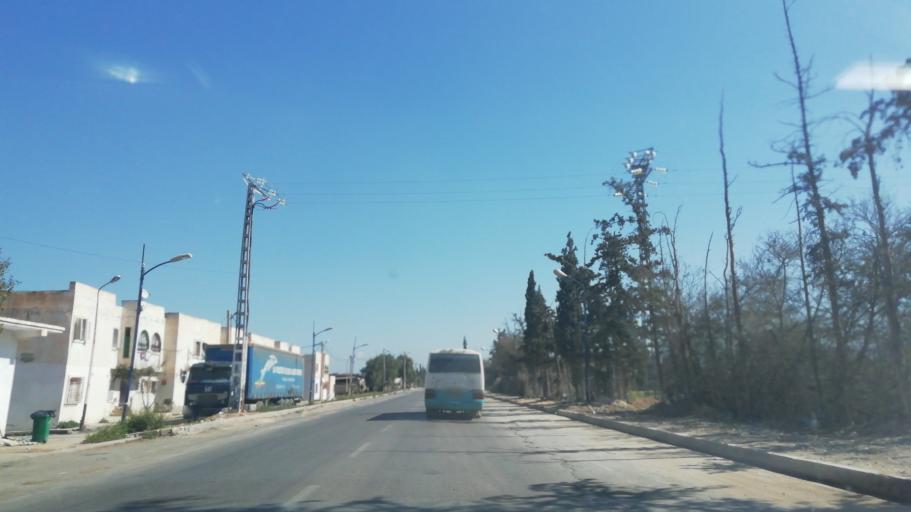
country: DZ
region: Mascara
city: Sig
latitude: 35.5702
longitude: -0.0424
